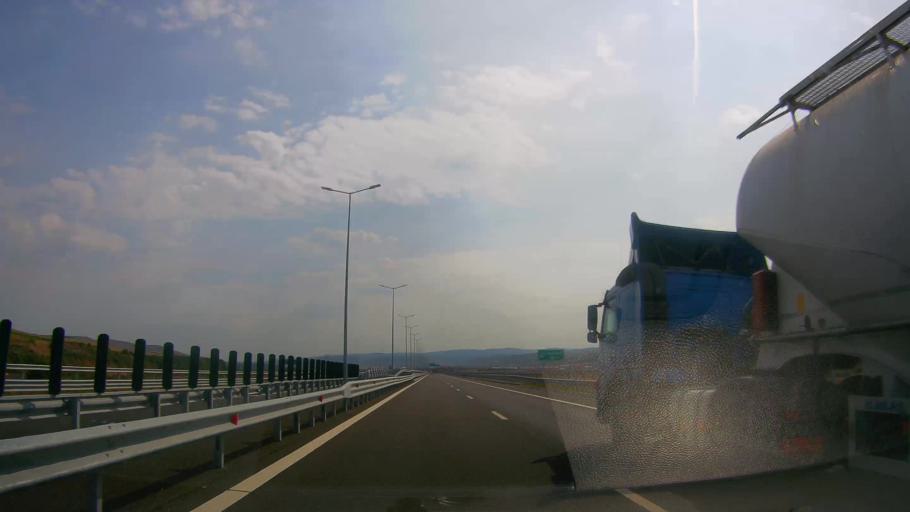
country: RO
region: Cluj
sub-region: Comuna Floresti
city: Luna de Sus
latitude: 46.7595
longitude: 23.4010
